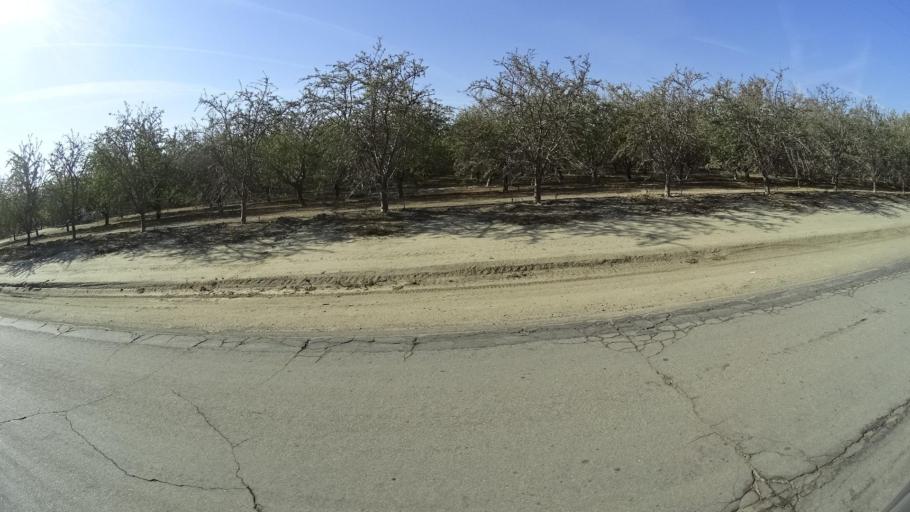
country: US
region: California
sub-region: Kern County
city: Wasco
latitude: 35.6563
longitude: -119.3486
